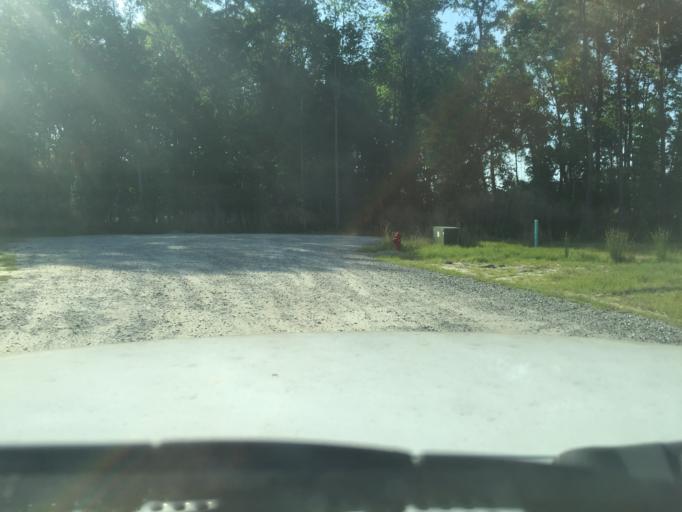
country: US
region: Georgia
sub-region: Chatham County
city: Georgetown
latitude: 32.0263
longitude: -81.2117
